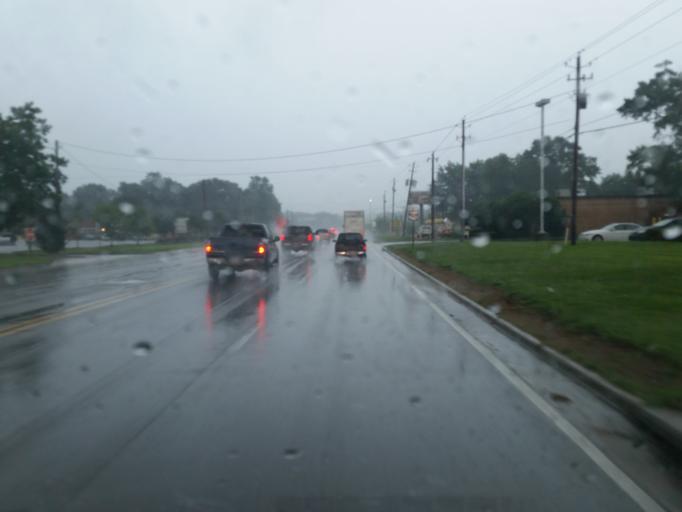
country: US
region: Alabama
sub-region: Mobile County
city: Prichard
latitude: 30.7786
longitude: -88.2587
